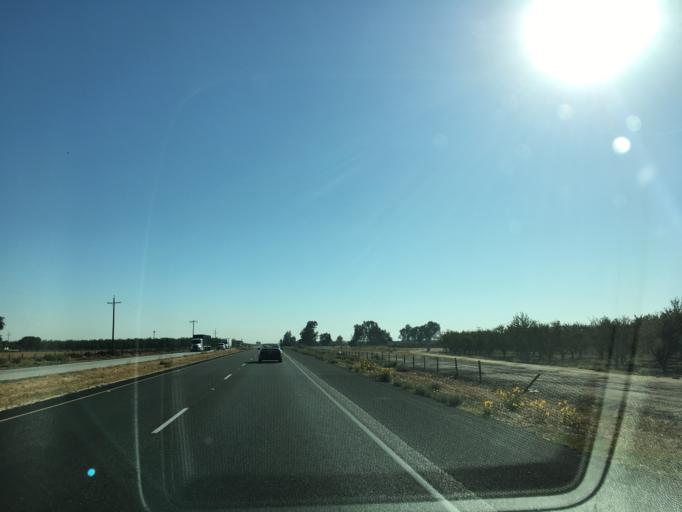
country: US
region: California
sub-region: Madera County
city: Chowchilla
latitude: 37.0834
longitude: -120.4420
